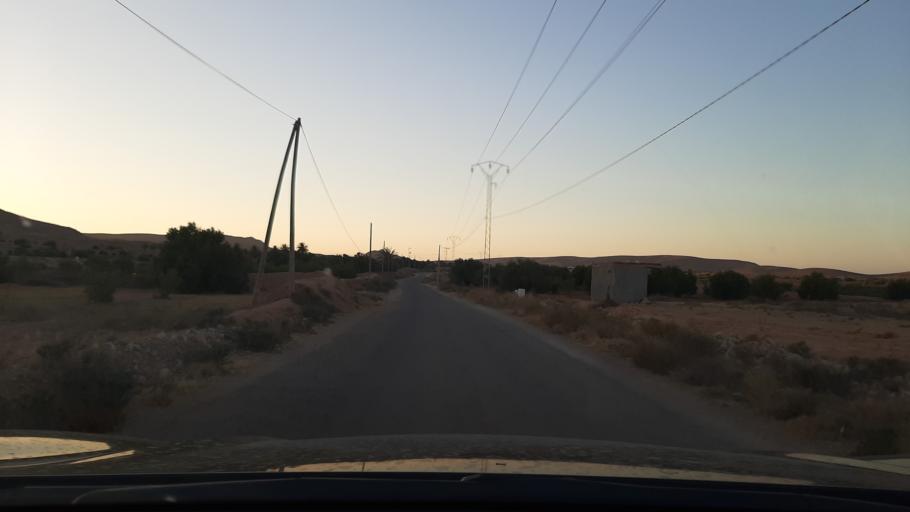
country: TN
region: Qabis
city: Matmata
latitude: 33.5514
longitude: 10.1878
